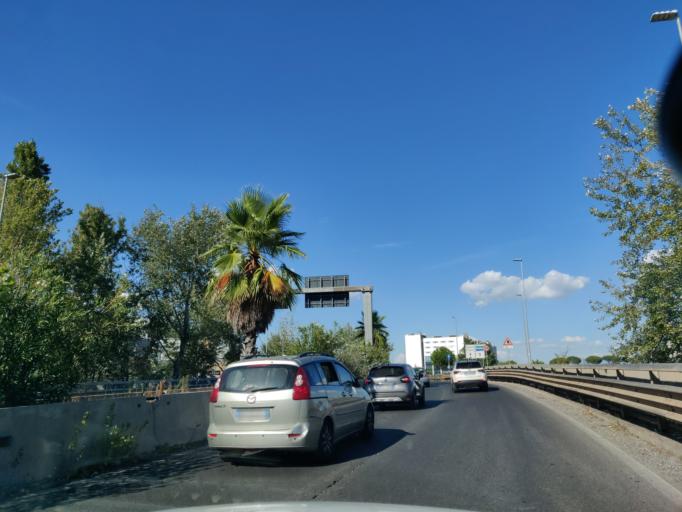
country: IT
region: Latium
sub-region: Citta metropolitana di Roma Capitale
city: Colle Verde
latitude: 41.9691
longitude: 12.5408
